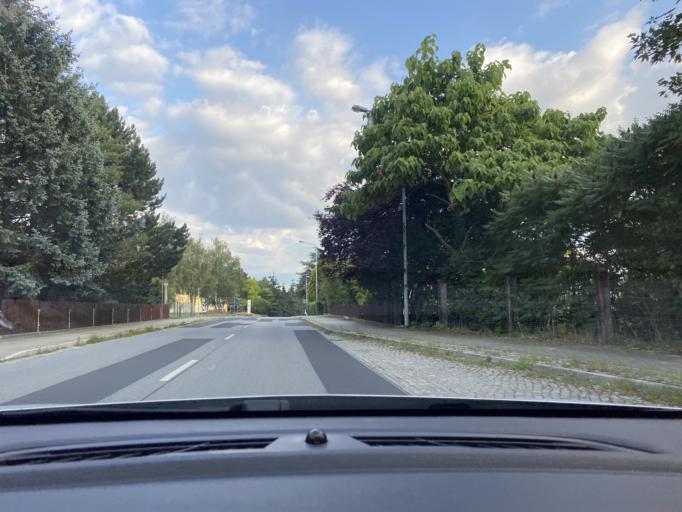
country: DE
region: Saxony
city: Radibor
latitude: 51.2235
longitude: 14.3873
